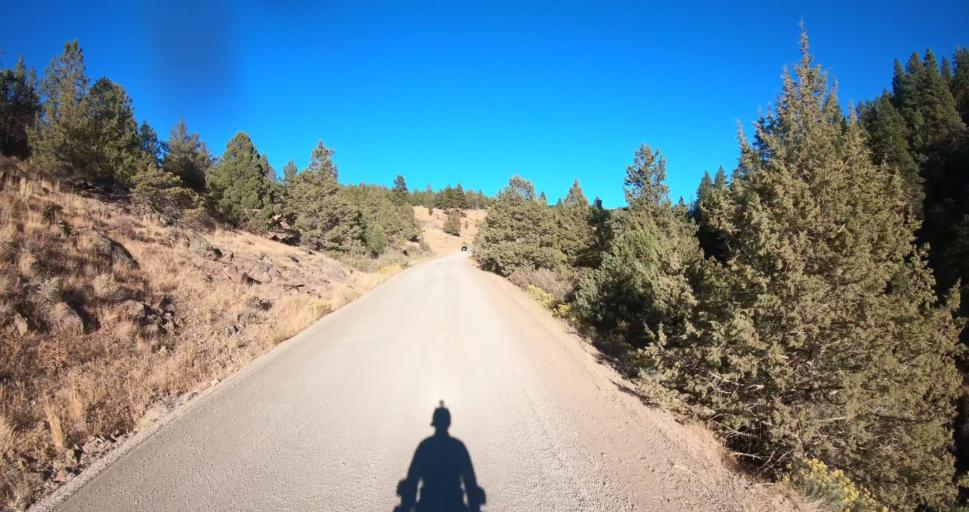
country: US
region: Oregon
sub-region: Lake County
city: Lakeview
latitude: 42.1930
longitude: -120.3192
